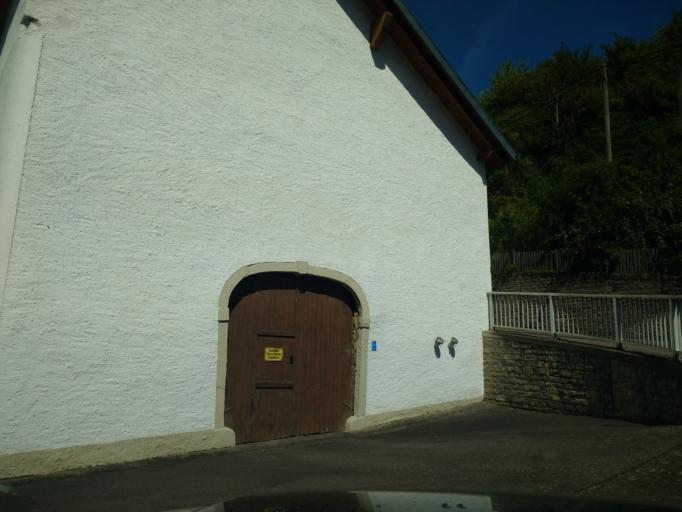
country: DE
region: Rheinland-Pfalz
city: Wincheringen
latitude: 49.6232
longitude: 6.4307
